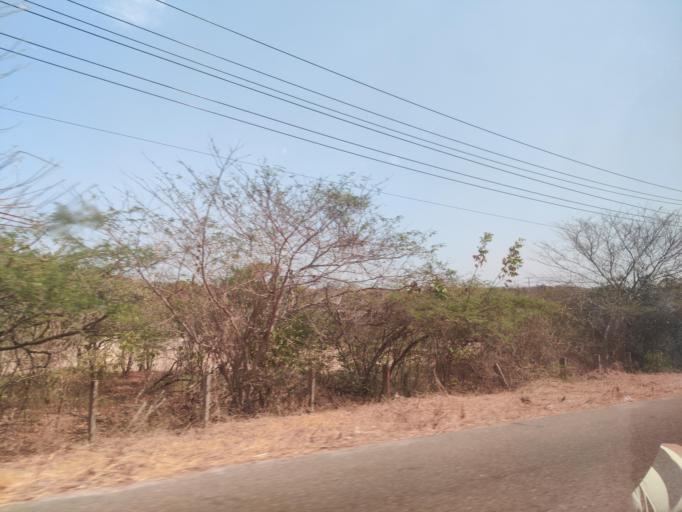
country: CO
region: Bolivar
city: Turbana
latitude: 10.2737
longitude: -75.5376
